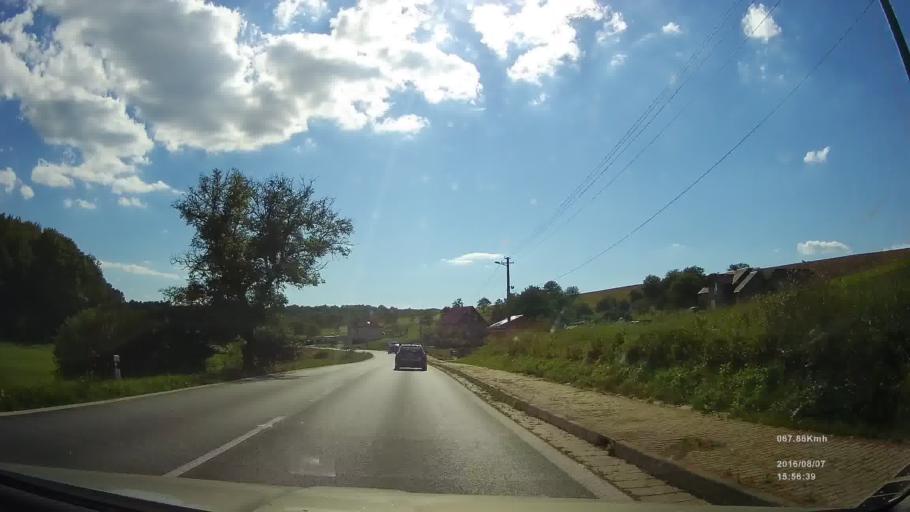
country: SK
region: Presovsky
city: Giraltovce
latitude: 49.0653
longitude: 21.4218
